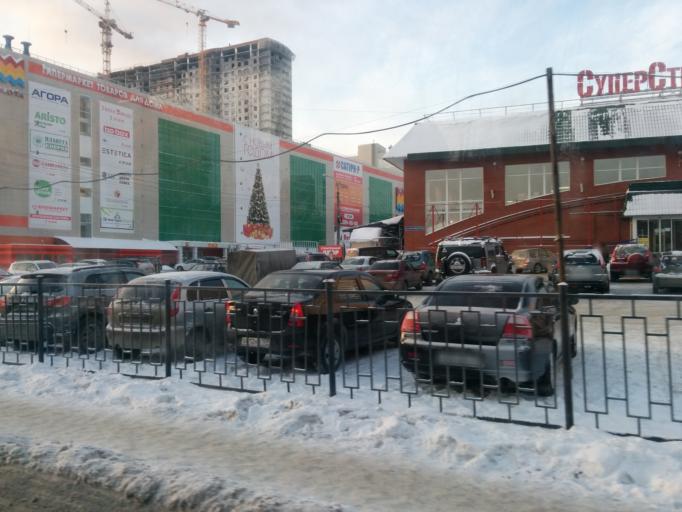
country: RU
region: Perm
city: Perm
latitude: 58.0032
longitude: 56.2681
